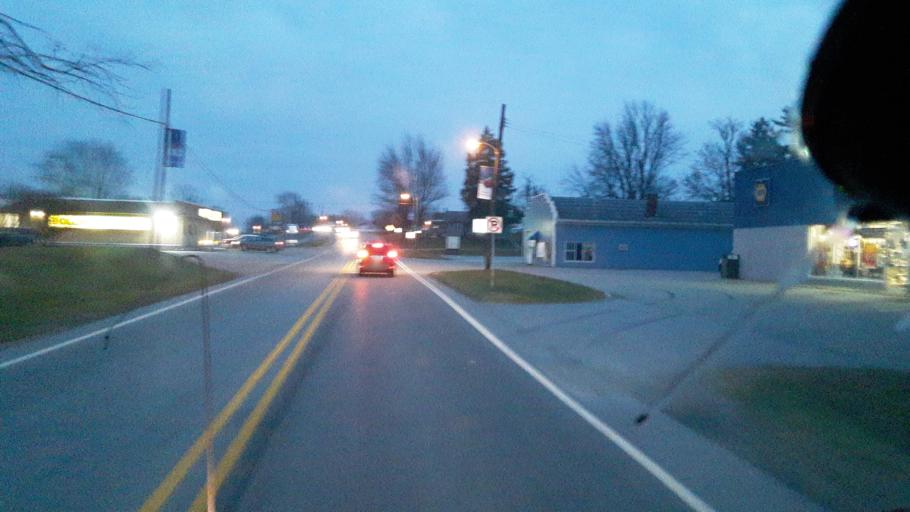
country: US
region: Indiana
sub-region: LaGrange County
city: Lagrange
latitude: 41.6371
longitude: -85.4178
